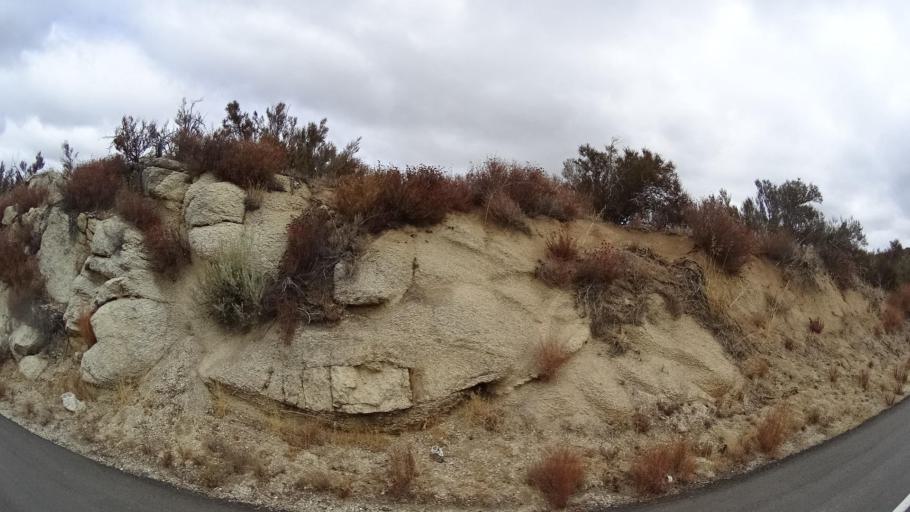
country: US
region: California
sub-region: San Diego County
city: Campo
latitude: 32.7222
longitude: -116.4106
